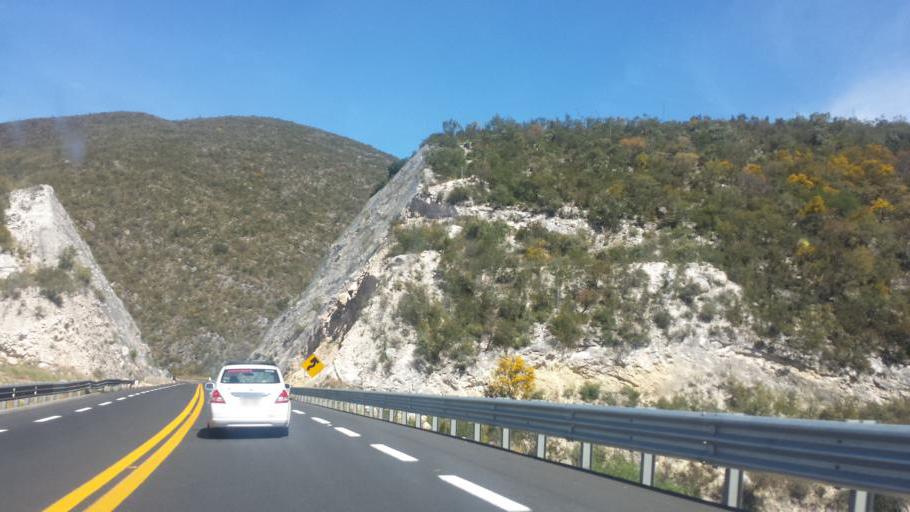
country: MX
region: Puebla
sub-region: San Jose Miahuatlan
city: San Pedro Tetitlan
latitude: 18.0229
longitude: -97.3489
